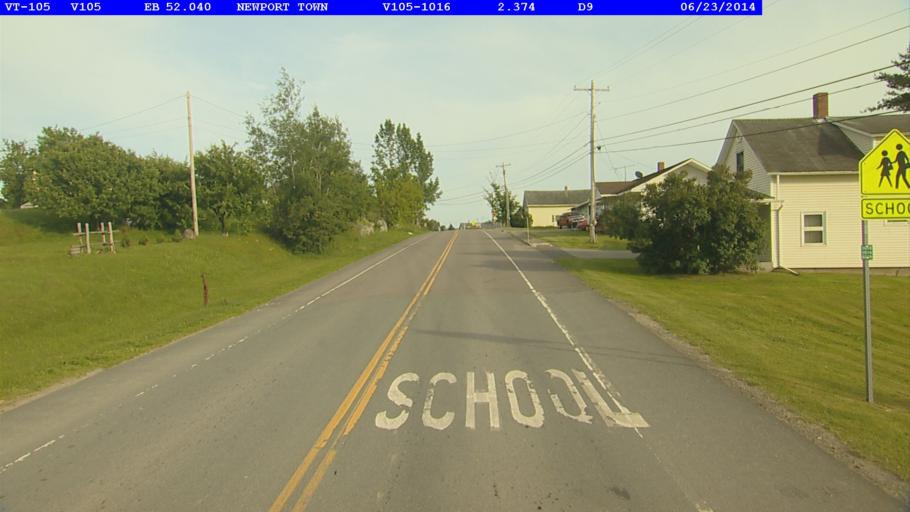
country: US
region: Vermont
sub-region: Orleans County
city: Newport
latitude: 44.9531
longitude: -72.3081
